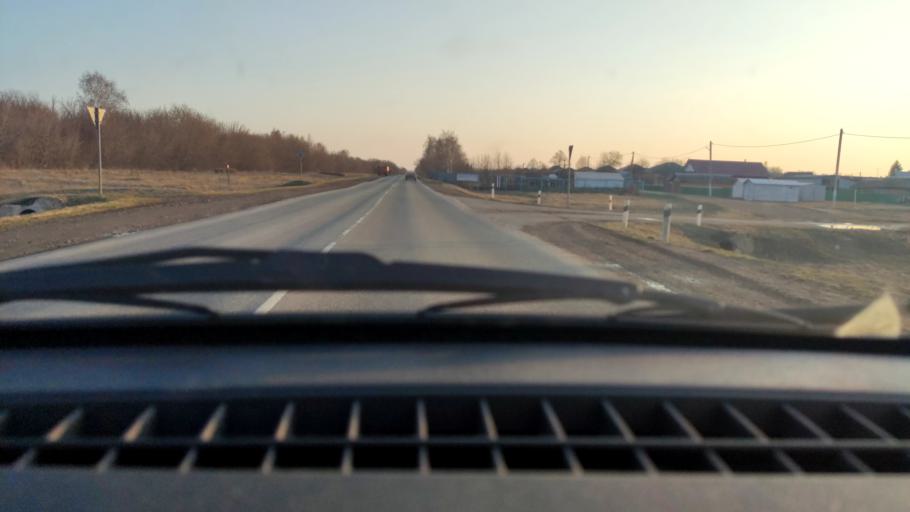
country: RU
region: Bashkortostan
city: Davlekanovo
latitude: 54.3009
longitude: 55.1324
